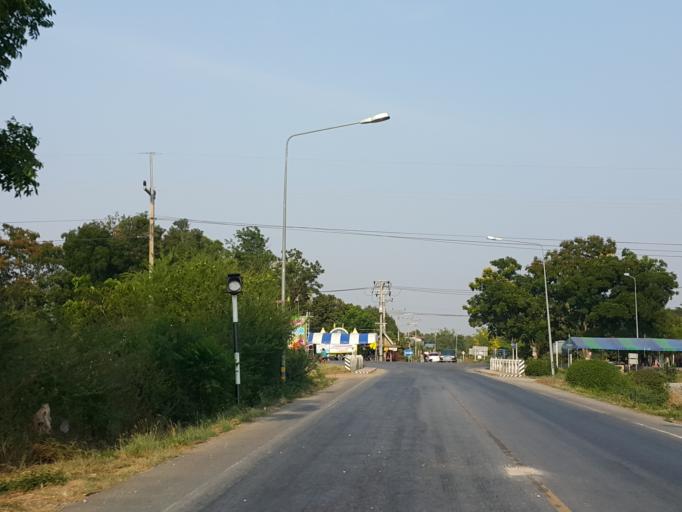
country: TH
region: Chai Nat
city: Sankhaburi
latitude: 15.0214
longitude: 100.1438
